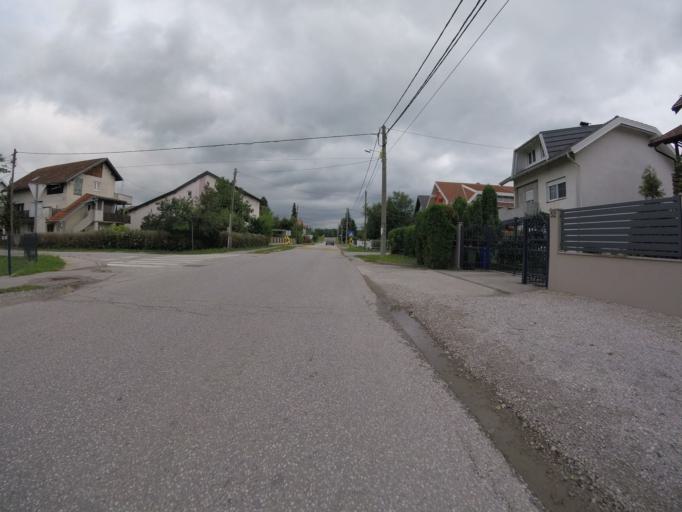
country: HR
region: Zagrebacka
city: Gradici
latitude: 45.7016
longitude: 16.0371
